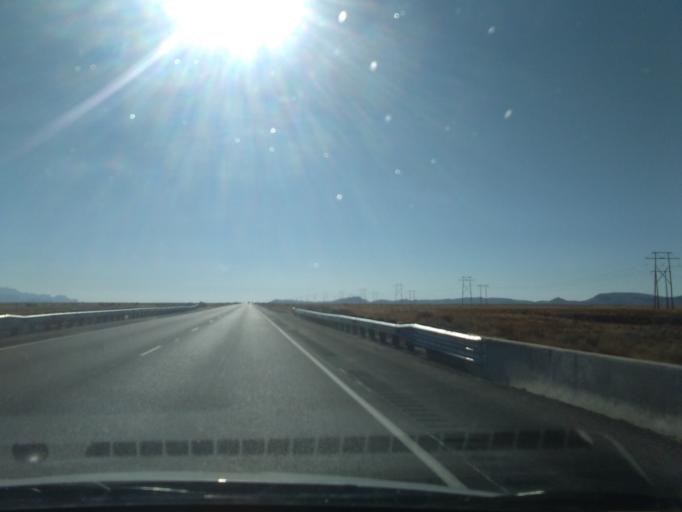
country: US
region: New Mexico
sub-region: Luna County
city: Deming
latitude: 32.4821
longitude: -107.5269
